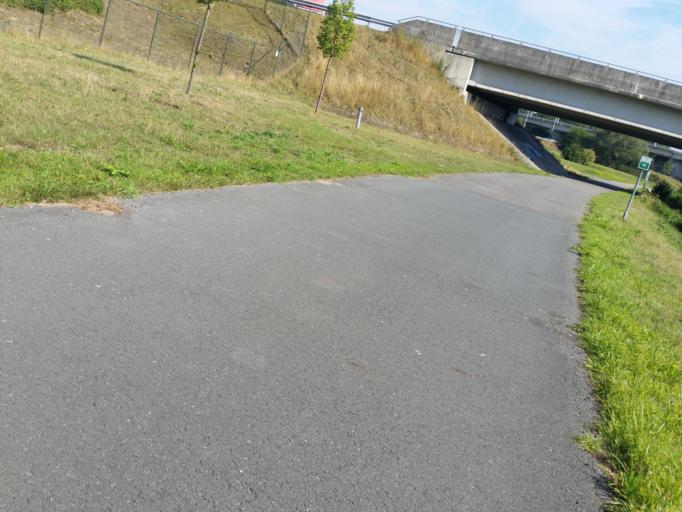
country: BE
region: Flanders
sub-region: Provincie Antwerpen
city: Mechelen
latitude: 51.0453
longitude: 4.4500
